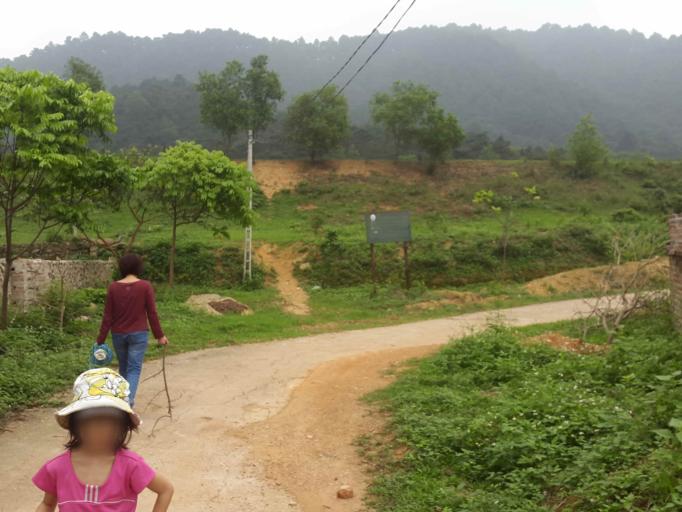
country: VN
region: Ha Noi
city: Soc Son
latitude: 21.2934
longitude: 105.7889
